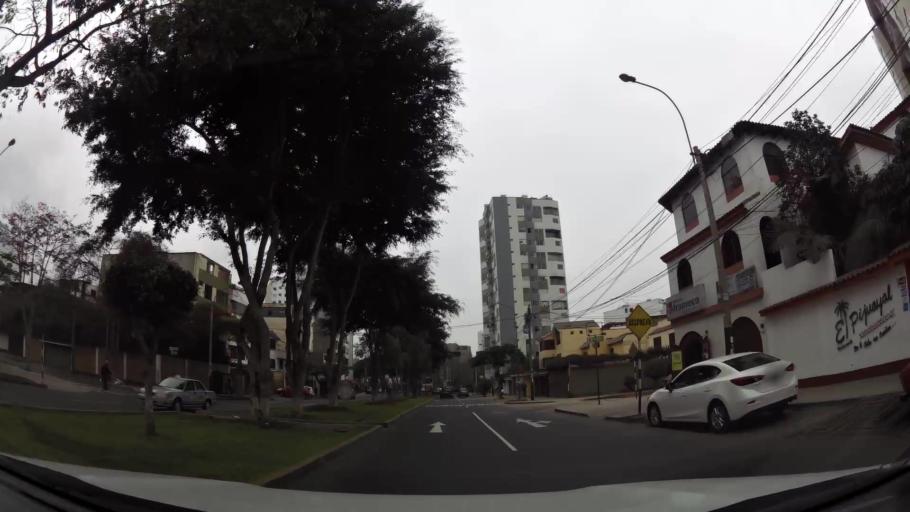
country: PE
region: Lima
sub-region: Lima
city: Surco
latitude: -12.1146
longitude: -77.0071
